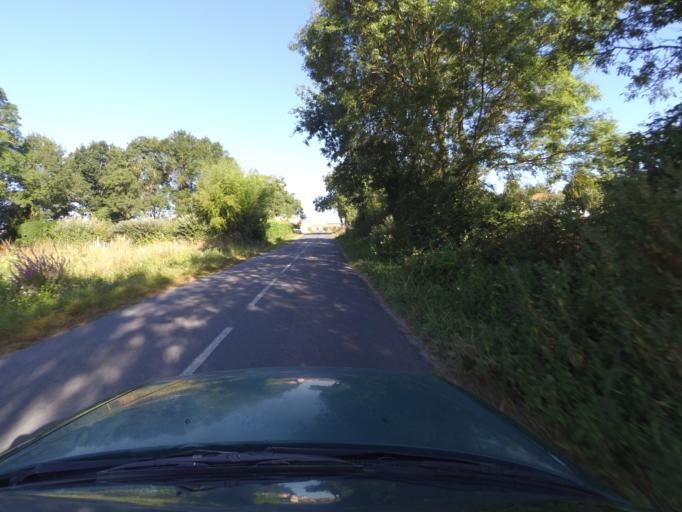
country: FR
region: Pays de la Loire
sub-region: Departement de la Loire-Atlantique
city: Le Bignon
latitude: 47.1049
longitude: -1.5078
